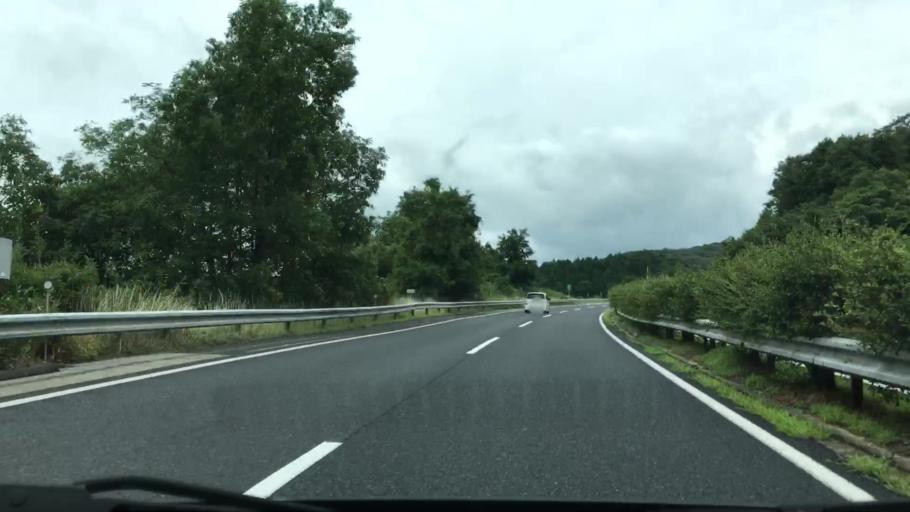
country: JP
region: Okayama
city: Tsuyama
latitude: 35.0174
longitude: 134.2192
